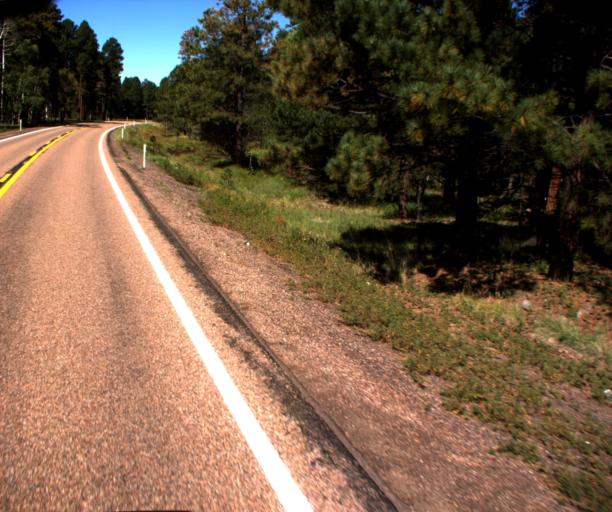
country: US
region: Arizona
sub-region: Navajo County
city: Pinetop-Lakeside
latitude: 34.0443
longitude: -109.7016
